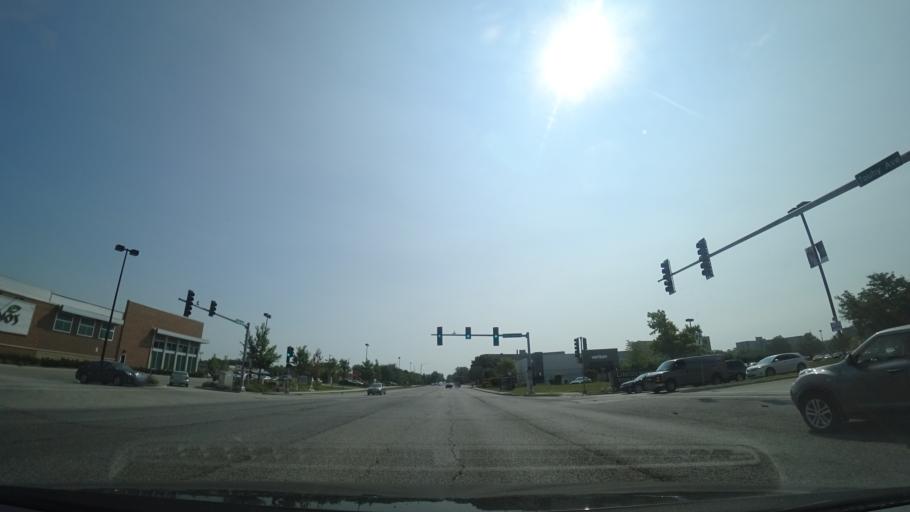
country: US
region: Illinois
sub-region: Cook County
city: Lincolnwood
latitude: 42.0118
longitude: -87.7146
